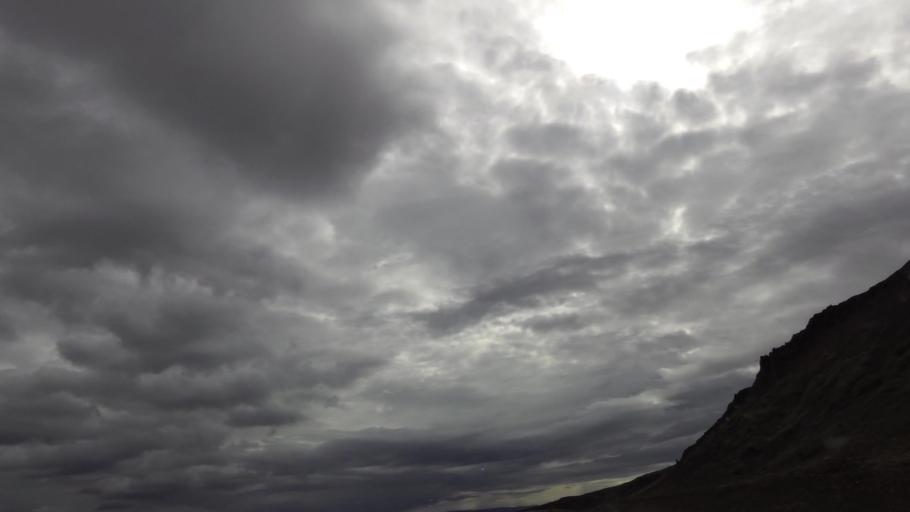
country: IS
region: West
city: Stykkisholmur
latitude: 65.5017
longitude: -22.1161
